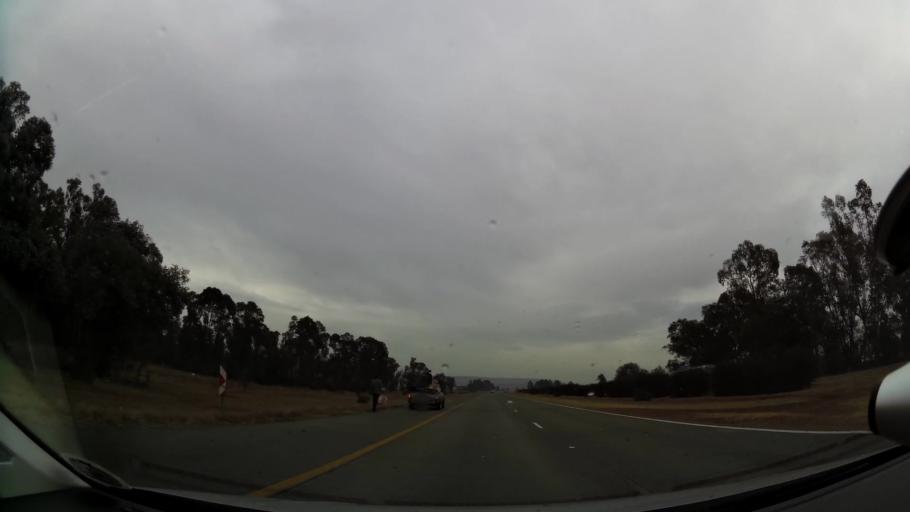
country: ZA
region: Gauteng
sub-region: City of Johannesburg Metropolitan Municipality
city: Soweto
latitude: -26.3344
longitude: 27.9340
